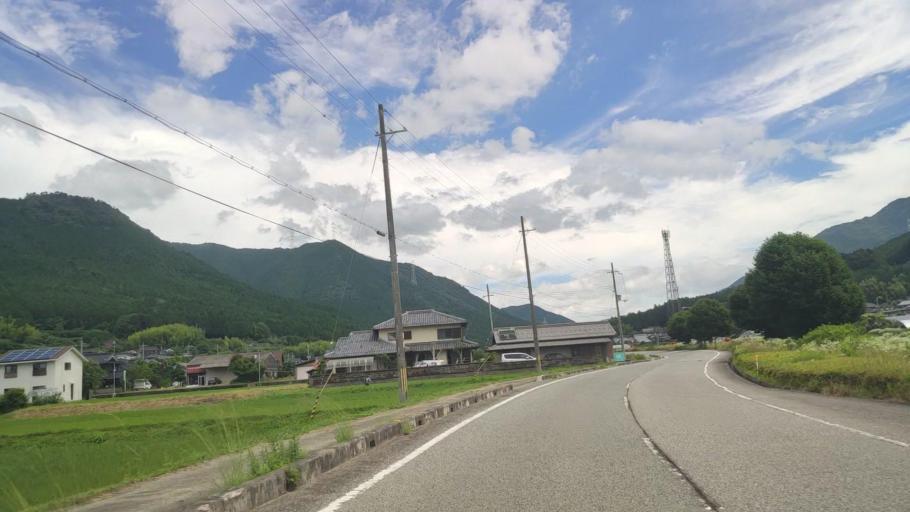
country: JP
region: Hyogo
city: Nishiwaki
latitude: 35.1431
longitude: 134.9260
